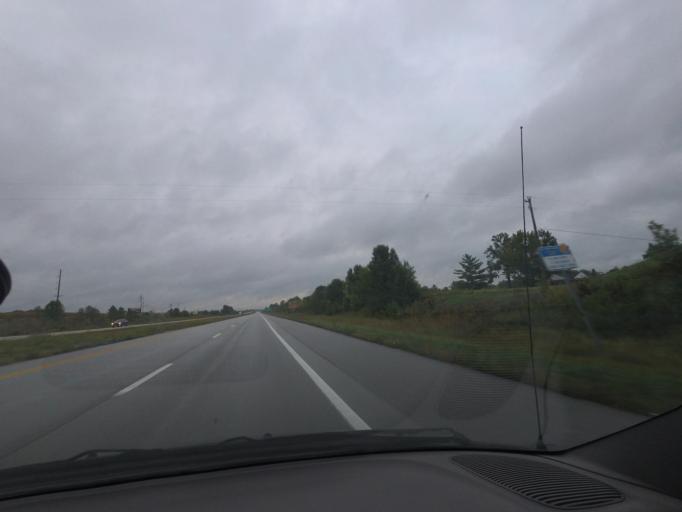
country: US
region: Missouri
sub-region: Marion County
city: Monroe City
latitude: 39.6648
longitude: -91.7348
